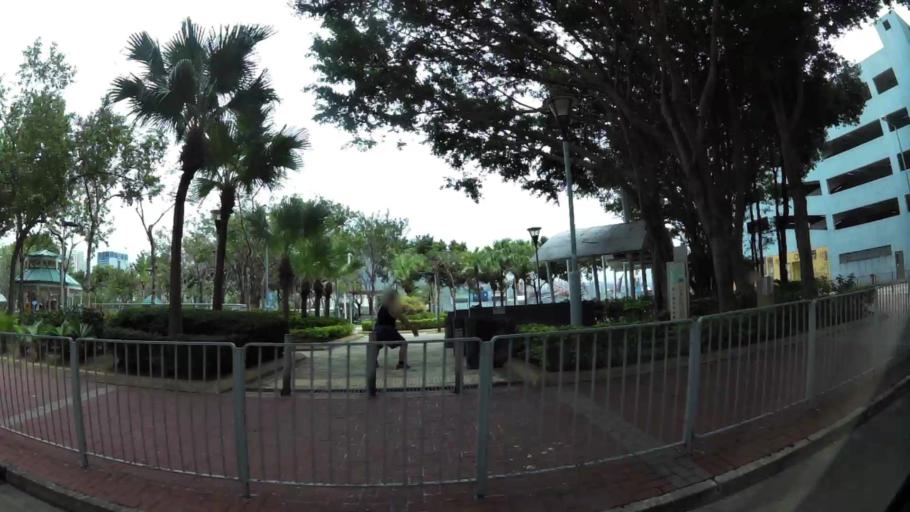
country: HK
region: Tuen Mun
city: Tuen Mun
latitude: 22.3746
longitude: 113.9689
